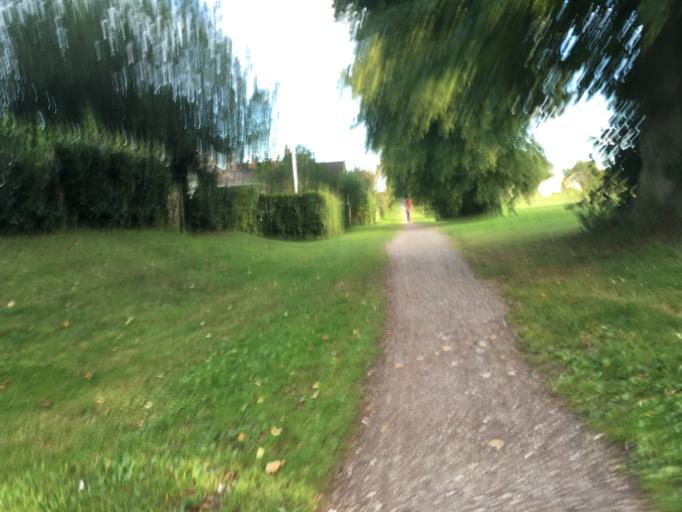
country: DK
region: Capital Region
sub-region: Hillerod Kommune
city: Hillerod
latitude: 55.9268
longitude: 12.2973
